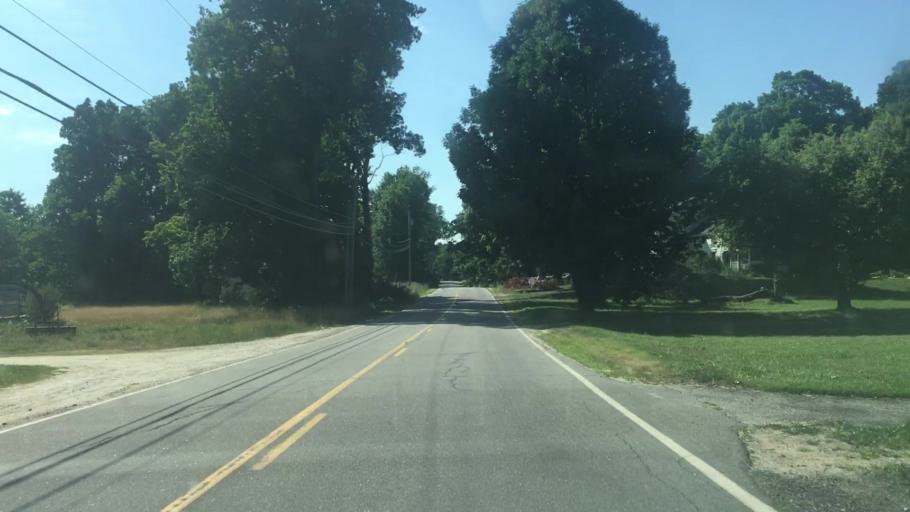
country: US
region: Maine
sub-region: York County
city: Hollis Center
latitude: 43.6317
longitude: -70.5641
